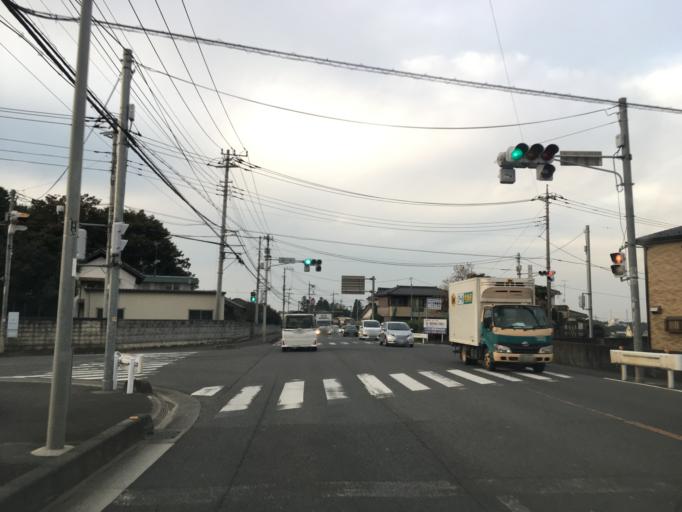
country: JP
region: Saitama
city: Sayama
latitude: 35.8737
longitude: 139.3796
